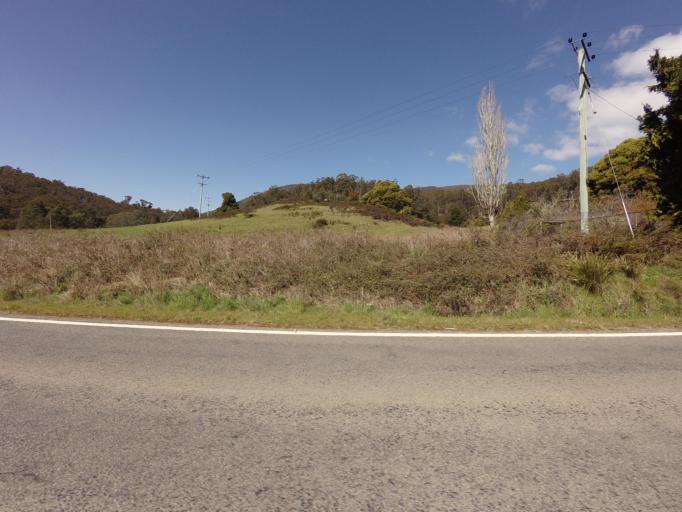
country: AU
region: Tasmania
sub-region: Derwent Valley
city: New Norfolk
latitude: -42.6821
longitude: 146.7278
